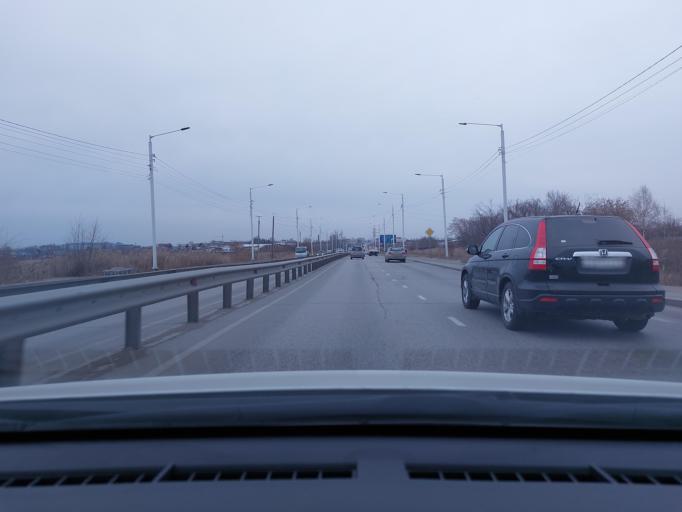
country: RU
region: Irkutsk
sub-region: Irkutskiy Rayon
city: Irkutsk
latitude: 52.3313
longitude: 104.2338
